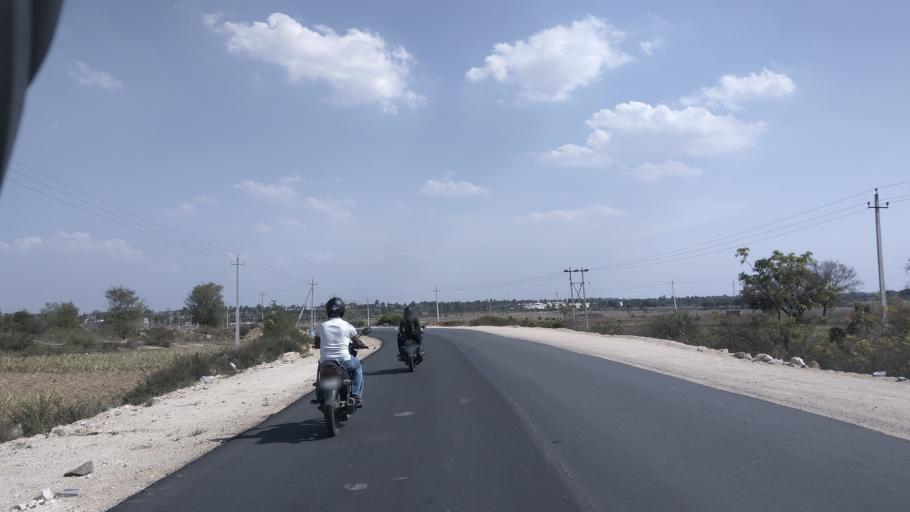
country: IN
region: Karnataka
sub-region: Kolar
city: Mulbagal
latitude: 13.1735
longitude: 78.3565
